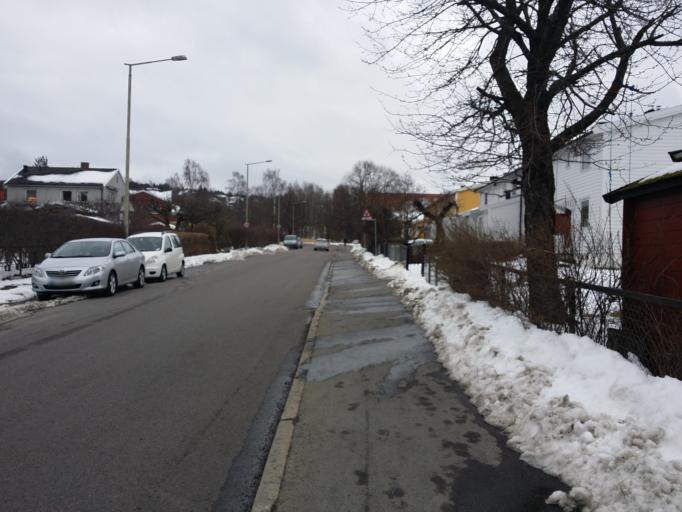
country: NO
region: Oslo
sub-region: Oslo
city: Oslo
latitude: 59.8962
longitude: 10.7837
